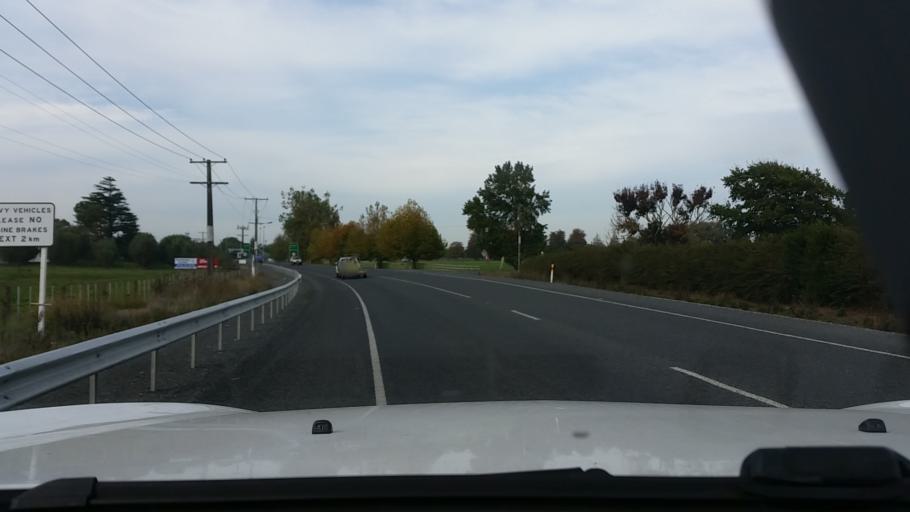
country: NZ
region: Waikato
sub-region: Hamilton City
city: Hamilton
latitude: -37.6674
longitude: 175.3007
